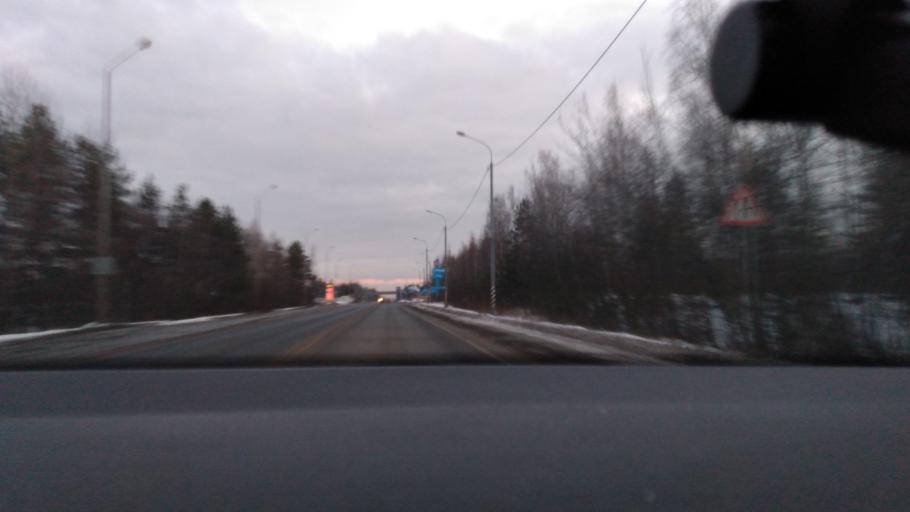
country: RU
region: Moskovskaya
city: Yegor'yevsk
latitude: 55.4199
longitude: 39.0412
